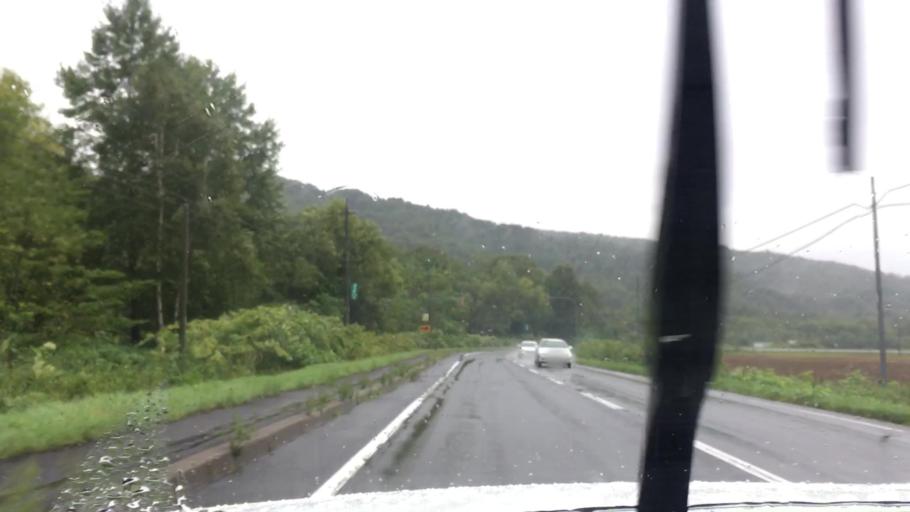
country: JP
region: Hokkaido
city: Niseko Town
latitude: 42.8026
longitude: 140.9915
